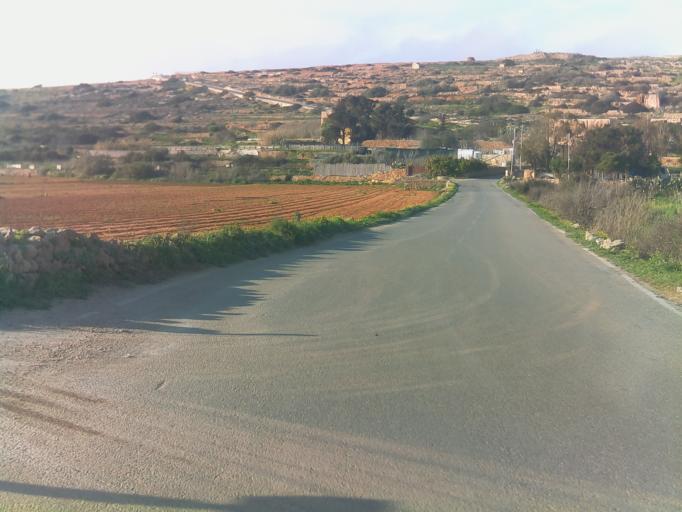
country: MT
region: Il-Mellieha
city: Mellieha
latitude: 35.9459
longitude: 14.3526
